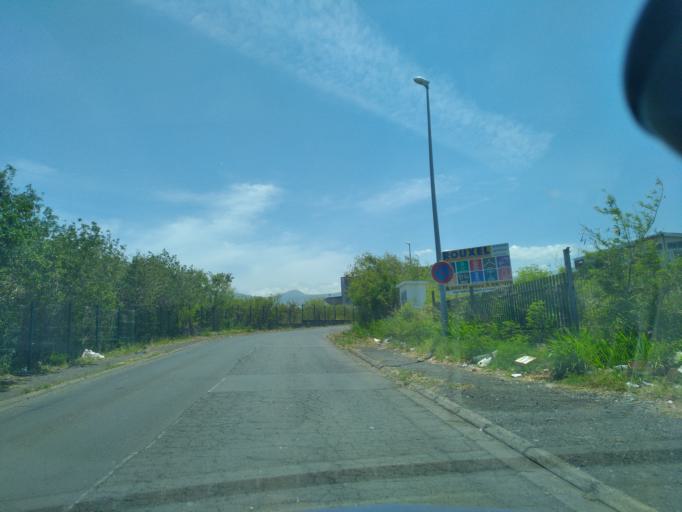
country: RE
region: Reunion
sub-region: Reunion
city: Saint-Pierre
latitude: -21.3210
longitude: 55.4494
